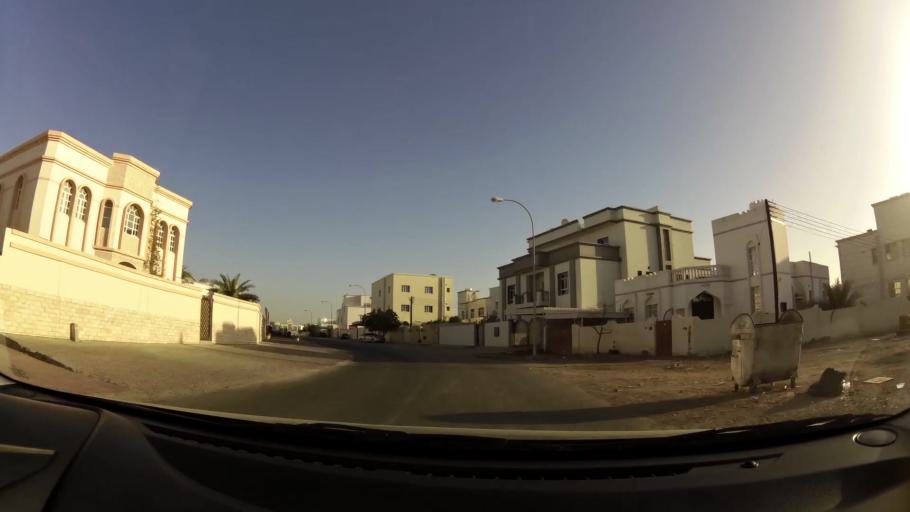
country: OM
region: Muhafazat Masqat
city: As Sib al Jadidah
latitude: 23.6100
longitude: 58.2356
